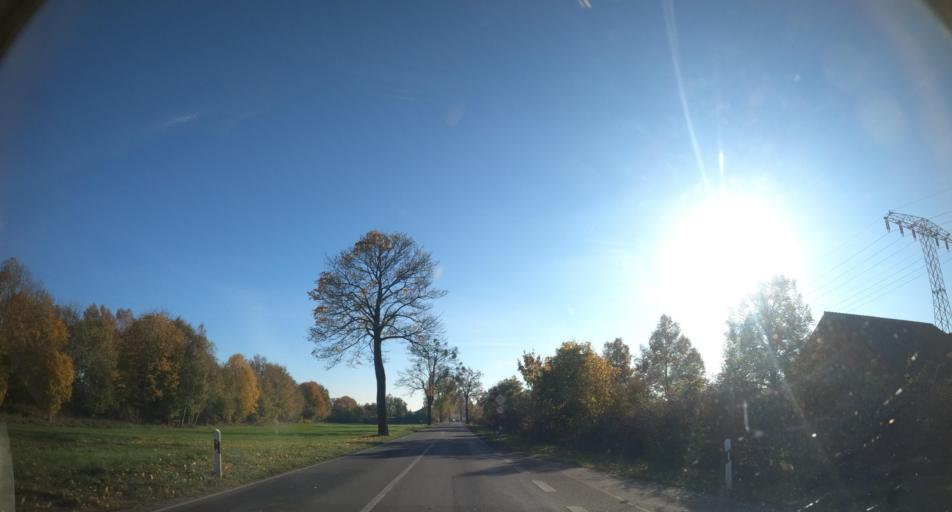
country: DE
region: Mecklenburg-Vorpommern
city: Ueckermunde
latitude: 53.7249
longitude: 14.0609
